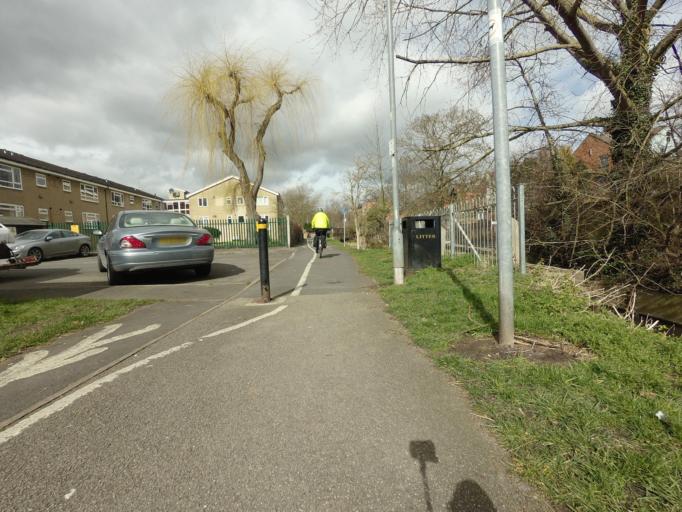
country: GB
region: England
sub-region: Lincolnshire
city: Grantham
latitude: 52.9092
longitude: -0.6357
